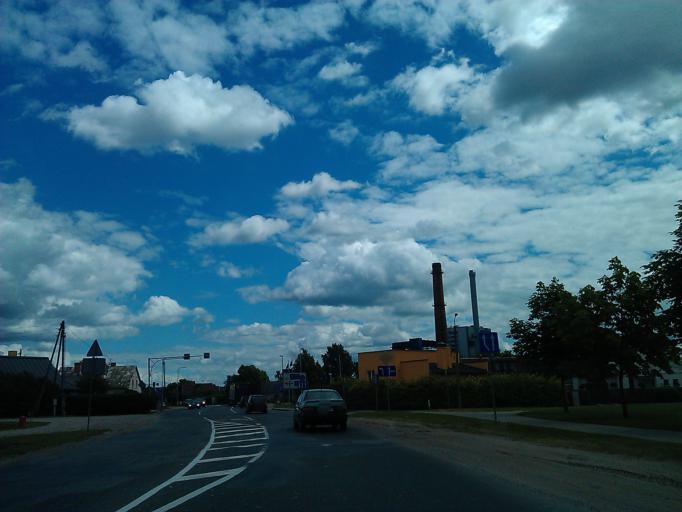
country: LV
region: Jelgava
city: Jelgava
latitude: 56.6371
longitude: 23.7058
